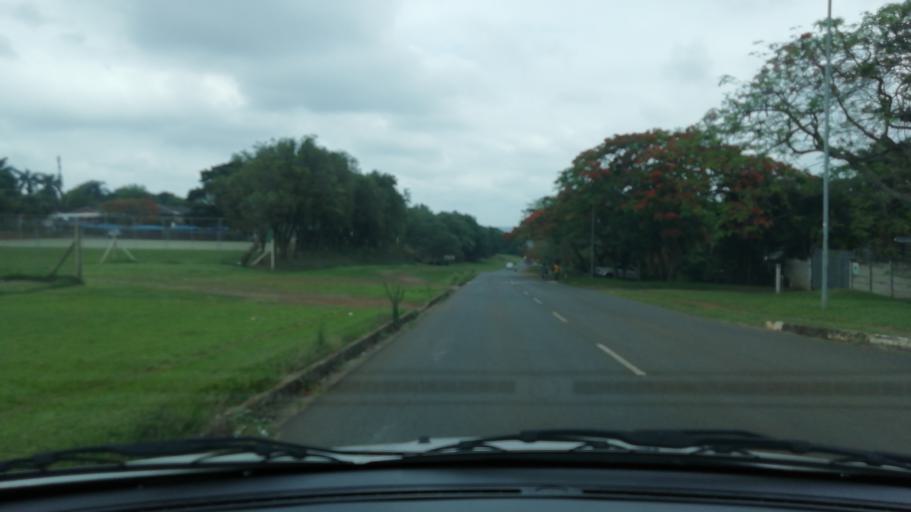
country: ZA
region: KwaZulu-Natal
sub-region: uThungulu District Municipality
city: Empangeni
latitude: -28.7520
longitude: 31.8851
